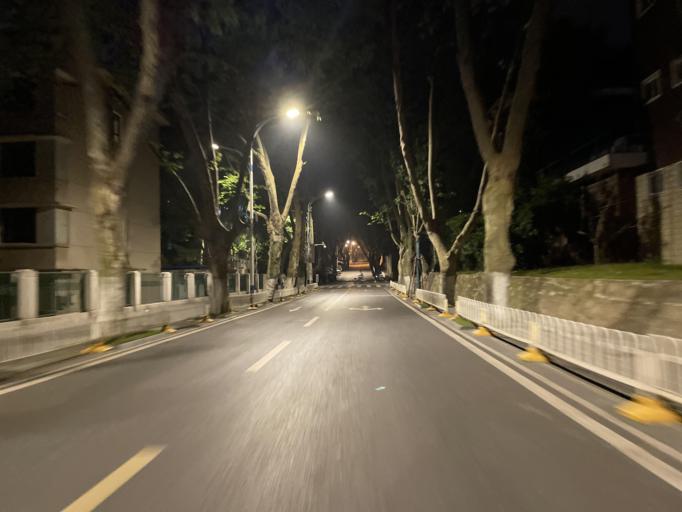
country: CN
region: Hubei
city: Guanshan
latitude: 30.5179
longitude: 114.4074
